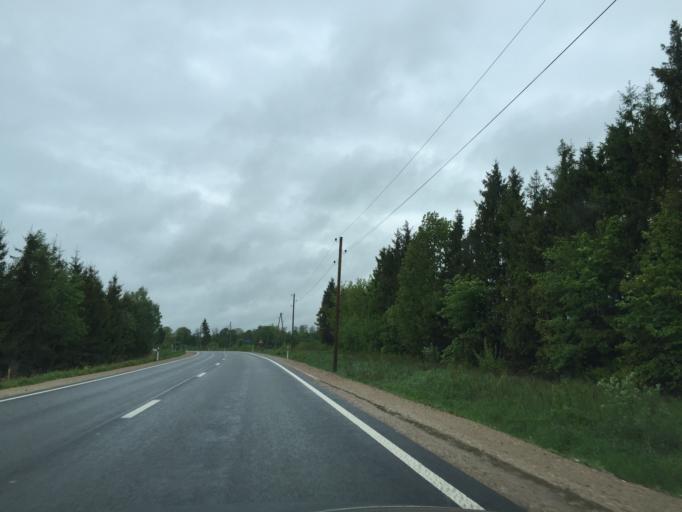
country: LV
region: Ogre
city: Jumprava
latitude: 56.6959
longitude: 24.8904
